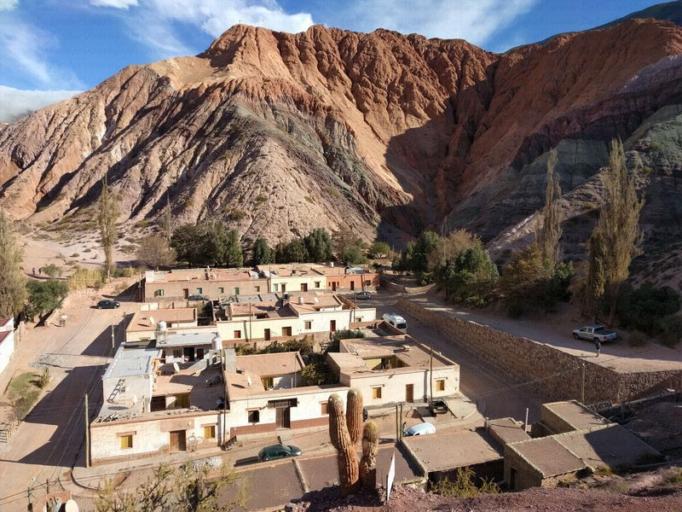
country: AR
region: Jujuy
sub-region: Departamento de Tumbaya
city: Tumbaya
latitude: -23.7456
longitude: -65.5016
